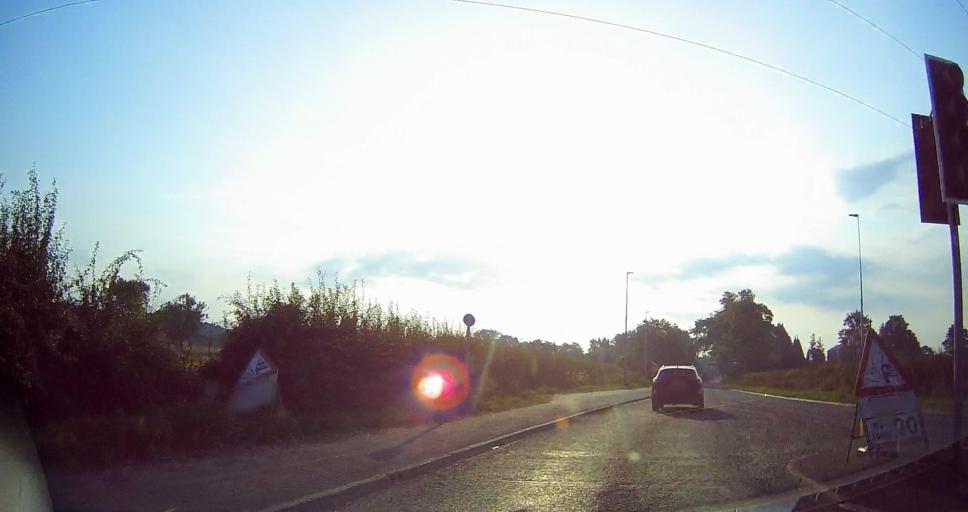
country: GB
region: England
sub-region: Cheshire East
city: Willaston
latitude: 53.0634
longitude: -2.4965
